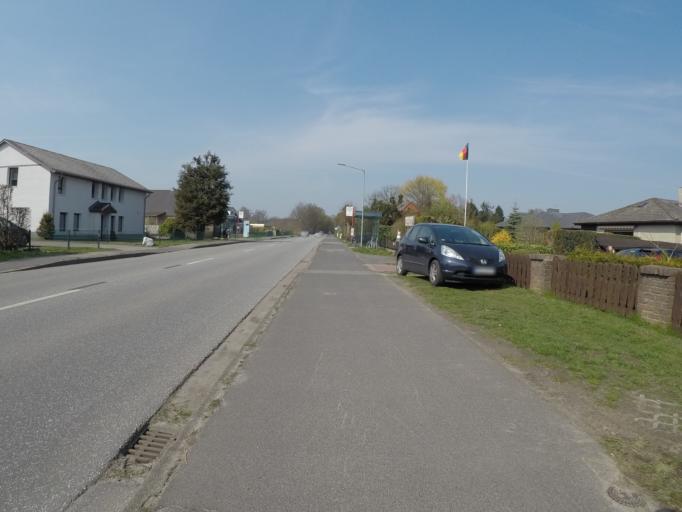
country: DE
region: Schleswig-Holstein
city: Kayhude
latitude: 53.7670
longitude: 10.1259
